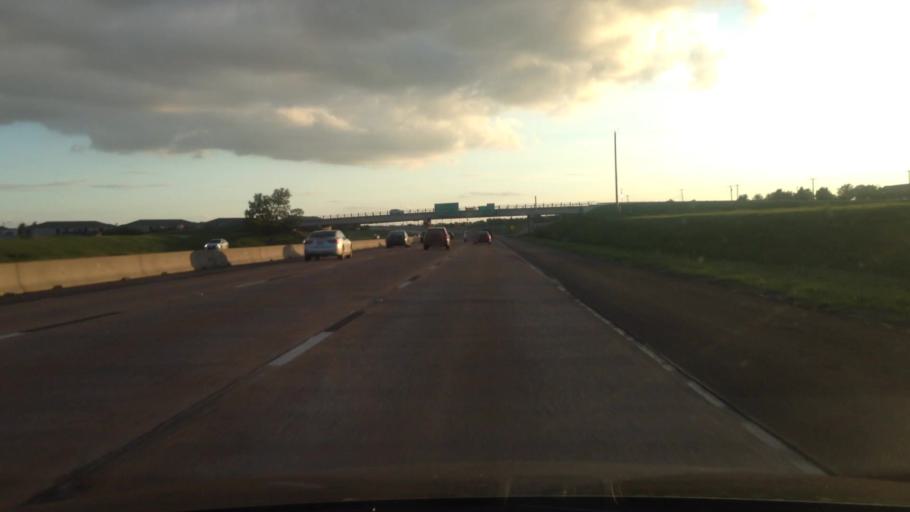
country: US
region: Texas
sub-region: Tarrant County
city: White Settlement
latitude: 32.7848
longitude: -97.4655
